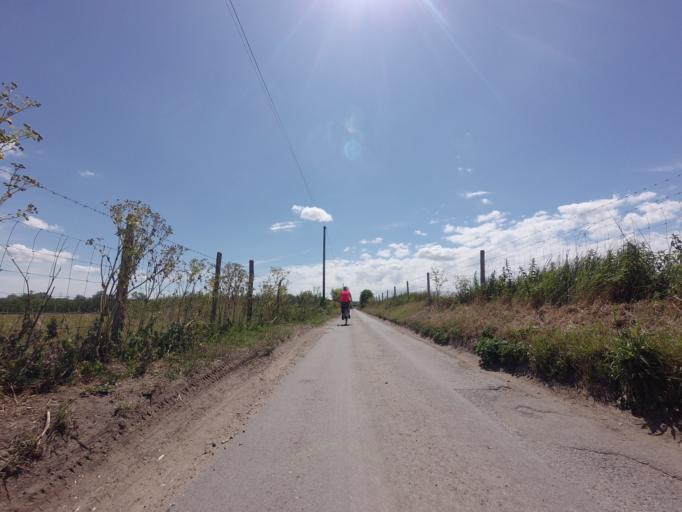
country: GB
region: England
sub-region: Medway
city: Cooling
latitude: 51.4588
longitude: 0.5137
